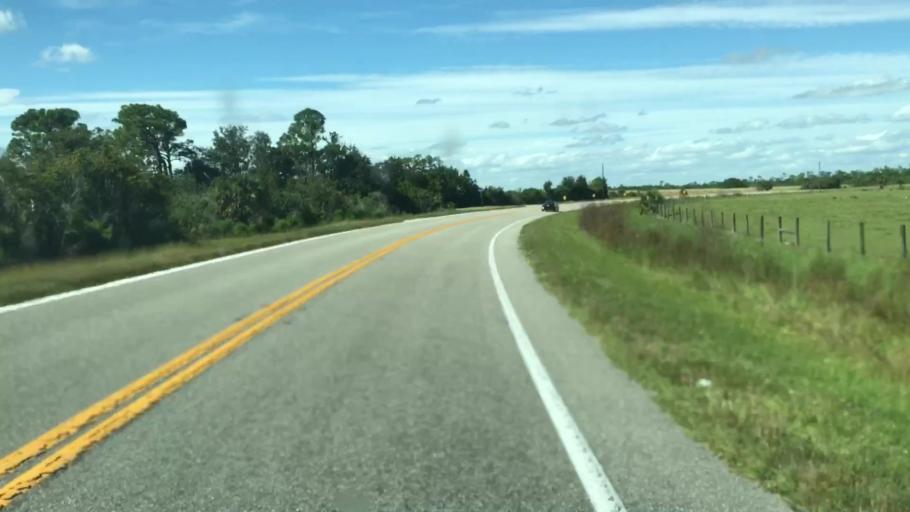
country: US
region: Florida
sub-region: Lee County
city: Olga
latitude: 26.7321
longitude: -81.7117
